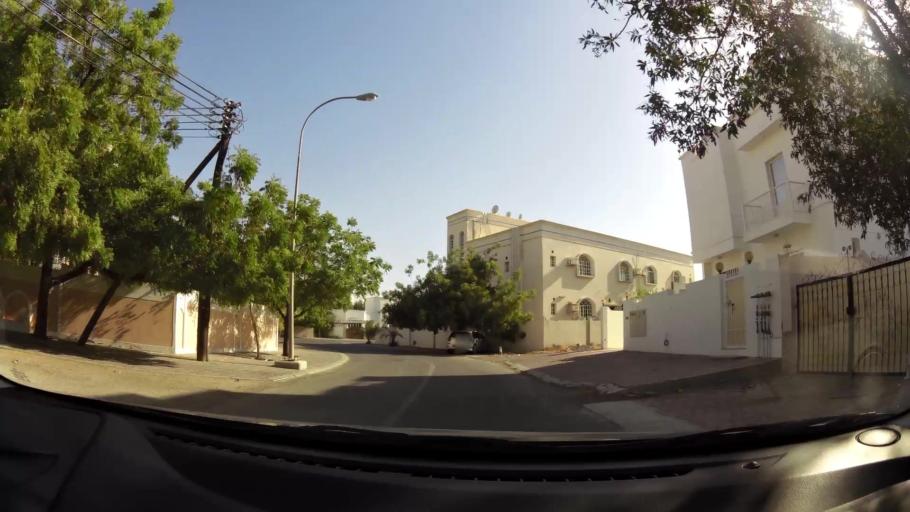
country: OM
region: Muhafazat Masqat
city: As Sib al Jadidah
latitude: 23.6163
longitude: 58.2114
